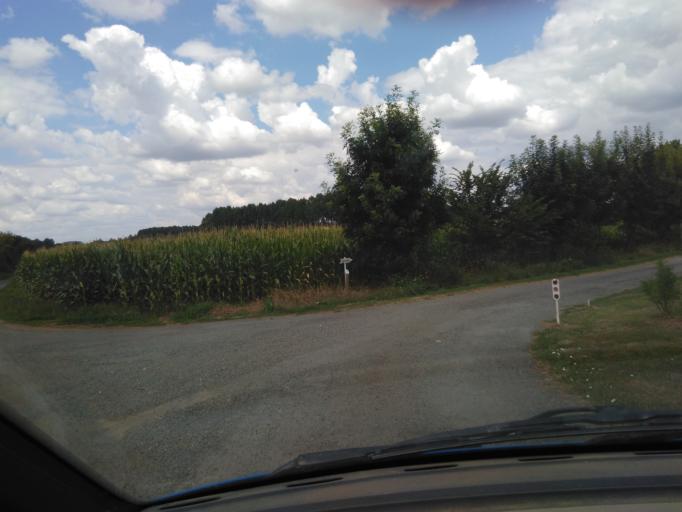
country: FR
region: Pays de la Loire
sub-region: Departement de la Vendee
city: Sainte-Hermine
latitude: 46.5559
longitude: -1.0274
